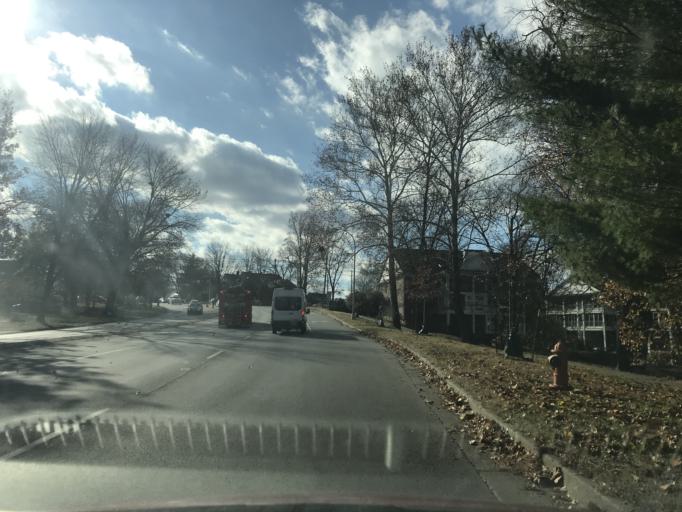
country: US
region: Kentucky
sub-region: Jefferson County
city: Audubon Park
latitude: 38.2249
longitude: -85.7291
